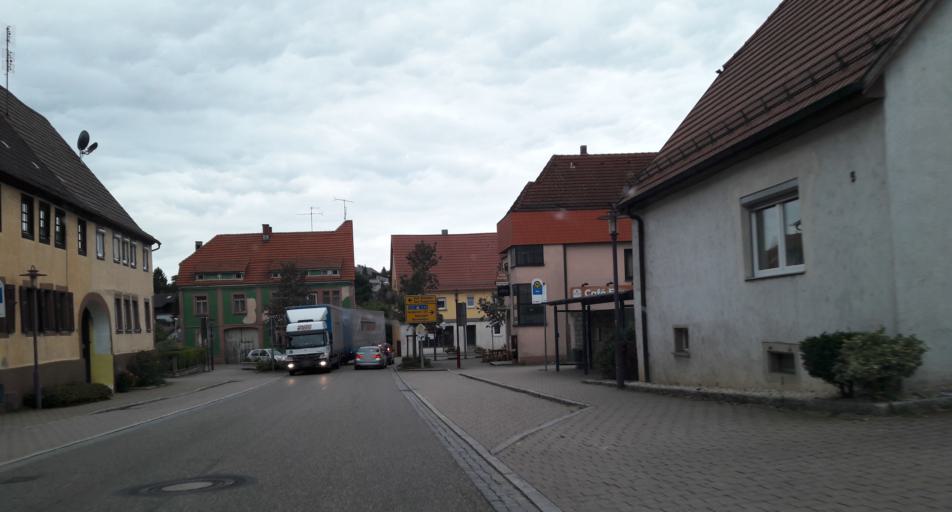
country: DE
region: Baden-Wuerttemberg
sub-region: Regierungsbezirk Stuttgart
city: Kirchardt
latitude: 49.2072
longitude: 8.9912
